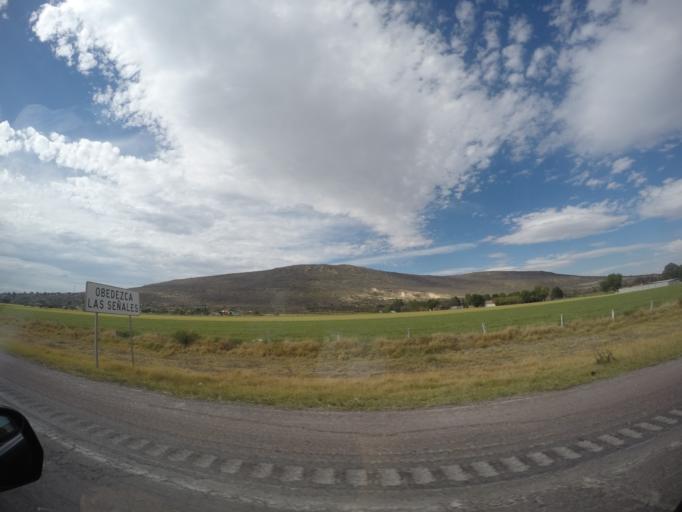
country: MX
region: Guanajuato
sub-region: Salamanca
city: Zapote de Palomas
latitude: 20.5895
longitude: -101.0988
